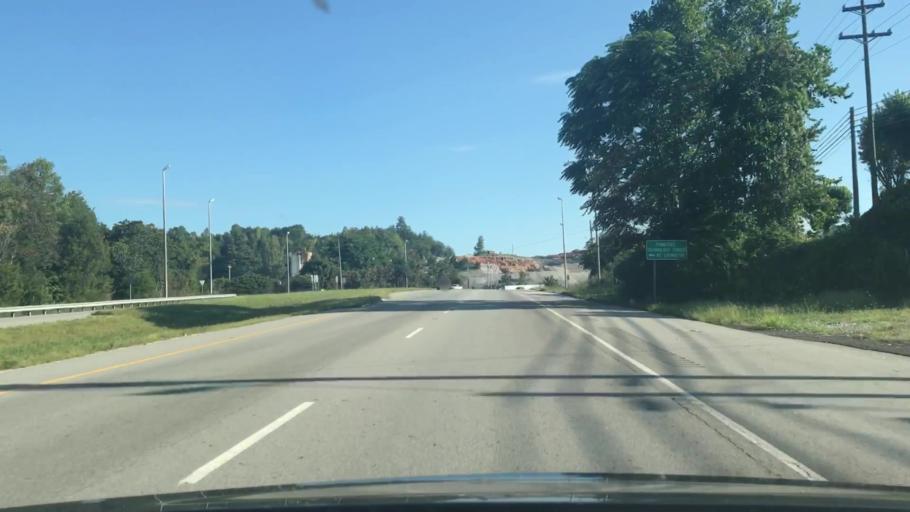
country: US
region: Tennessee
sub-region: Overton County
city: Livingston
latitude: 36.3955
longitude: -85.3018
